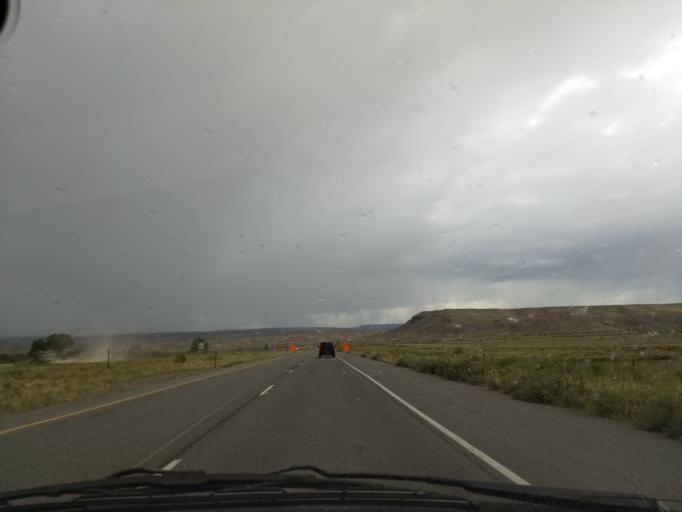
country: US
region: Colorado
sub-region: Delta County
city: Delta
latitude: 38.7577
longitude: -108.1458
